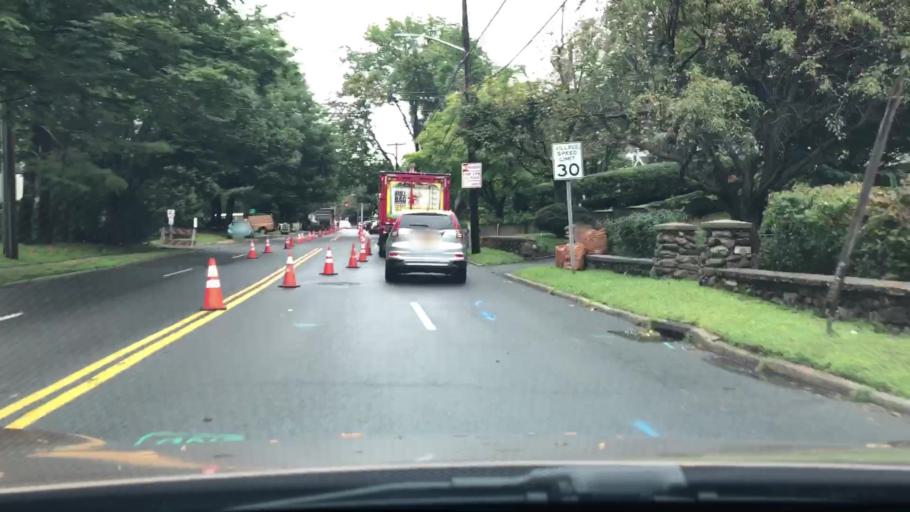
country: US
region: New York
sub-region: Westchester County
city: Greenville
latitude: 40.9796
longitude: -73.8011
